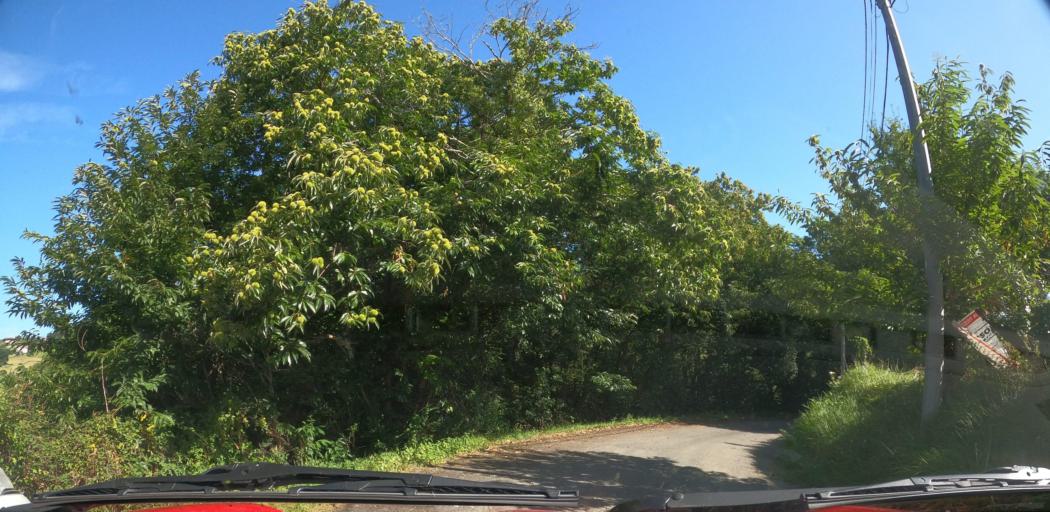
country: FR
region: Aquitaine
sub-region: Departement des Pyrenees-Atlantiques
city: Sare
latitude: 43.3142
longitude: -1.5796
